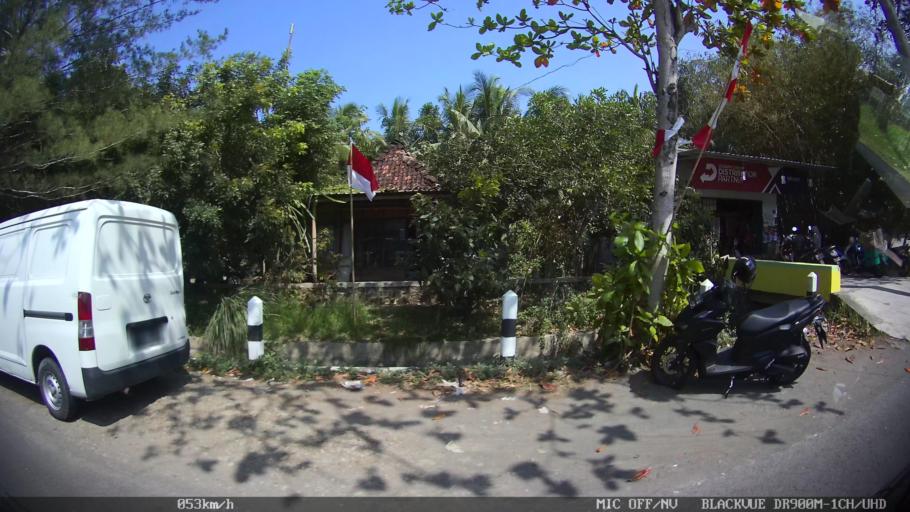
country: ID
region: Daerah Istimewa Yogyakarta
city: Srandakan
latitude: -7.9061
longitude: 110.1521
